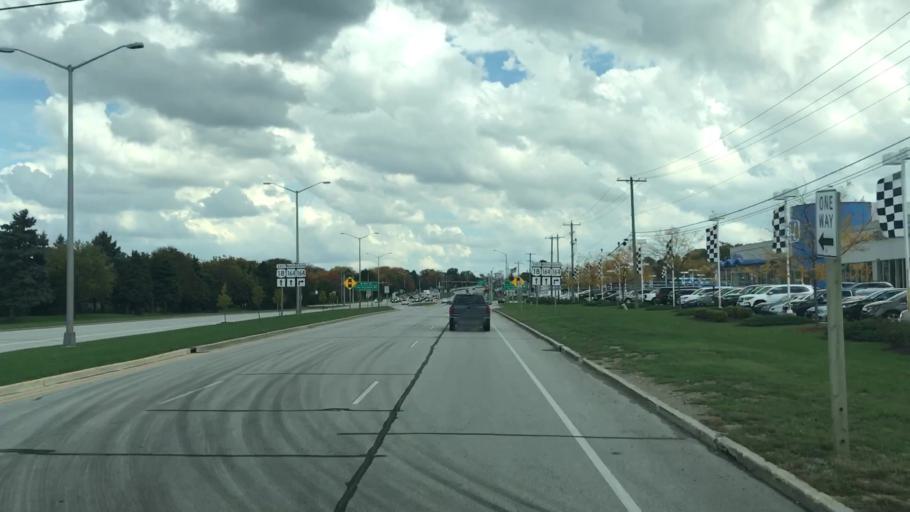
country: US
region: Wisconsin
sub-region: Waukesha County
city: Waukesha
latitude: 43.0254
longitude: -88.2026
